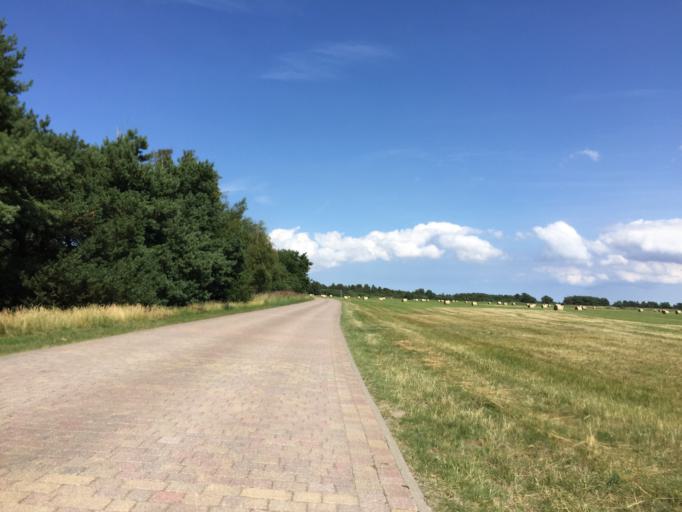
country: DE
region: Mecklenburg-Vorpommern
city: Hiddensee
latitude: 54.5364
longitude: 13.0932
